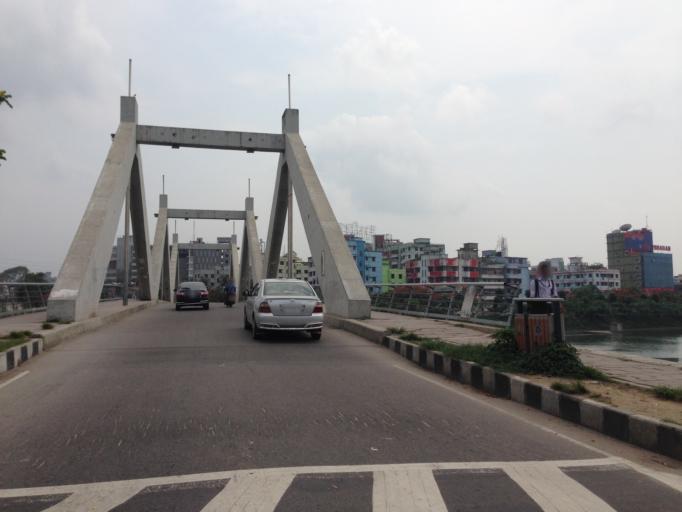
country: BD
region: Dhaka
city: Paltan
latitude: 23.7691
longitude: 90.4227
